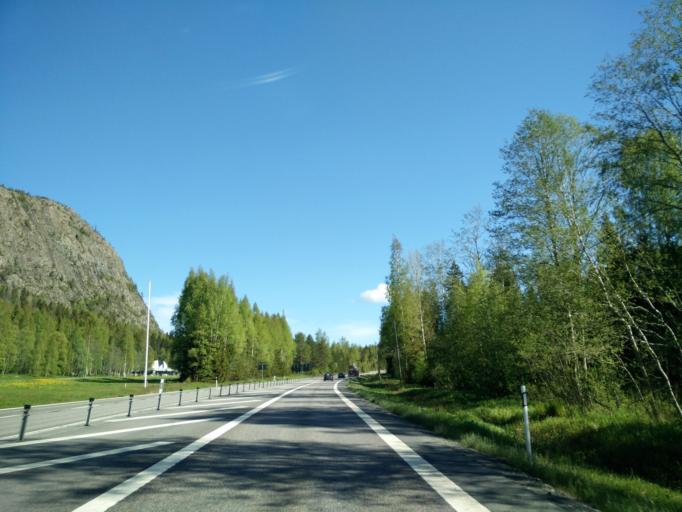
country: SE
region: Vaesternorrland
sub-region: Kramfors Kommun
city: Nordingra
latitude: 63.0691
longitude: 18.3571
